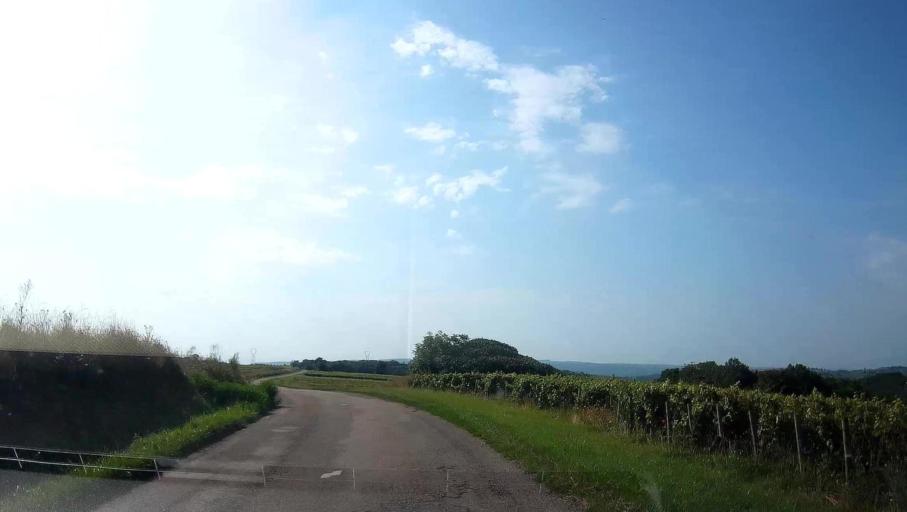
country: FR
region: Bourgogne
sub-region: Departement de Saone-et-Loire
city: Couches
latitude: 46.9013
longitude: 4.5989
